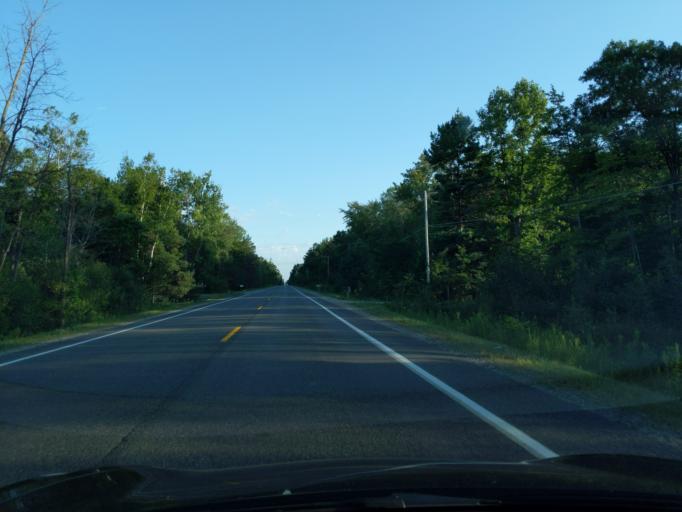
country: US
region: Michigan
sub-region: Midland County
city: Midland
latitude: 43.5368
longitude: -84.3698
